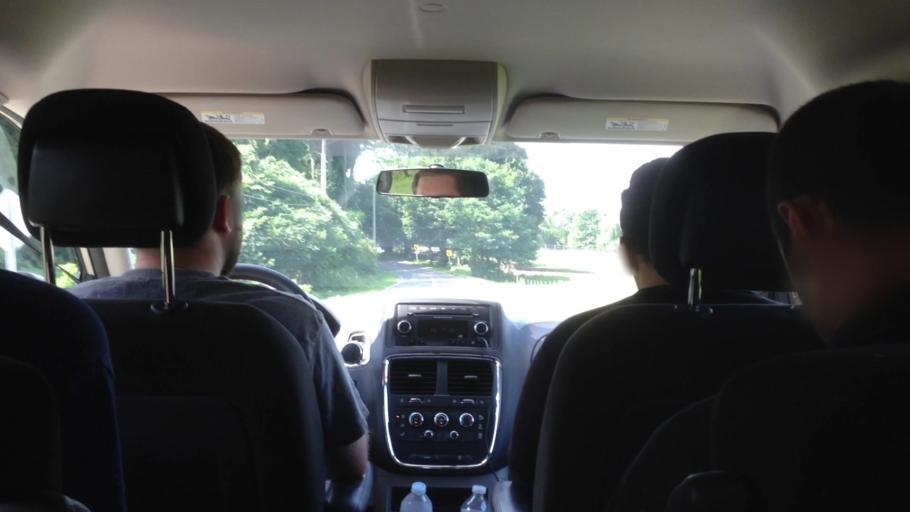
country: US
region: New York
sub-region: Dutchess County
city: Tivoli
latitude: 42.0527
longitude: -73.8785
